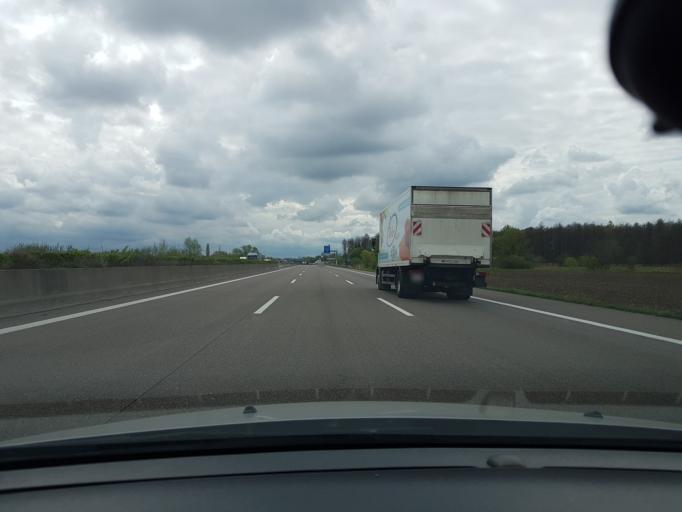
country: DE
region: Baden-Wuerttemberg
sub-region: Freiburg Region
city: Appenweier
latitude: 48.5685
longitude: 7.9603
